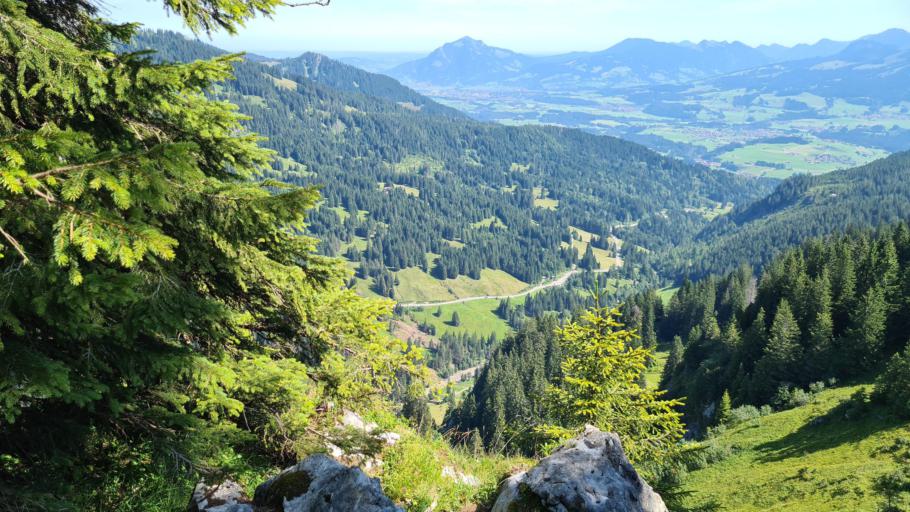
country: DE
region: Bavaria
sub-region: Swabia
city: Obermaiselstein
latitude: 47.4252
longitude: 10.1876
